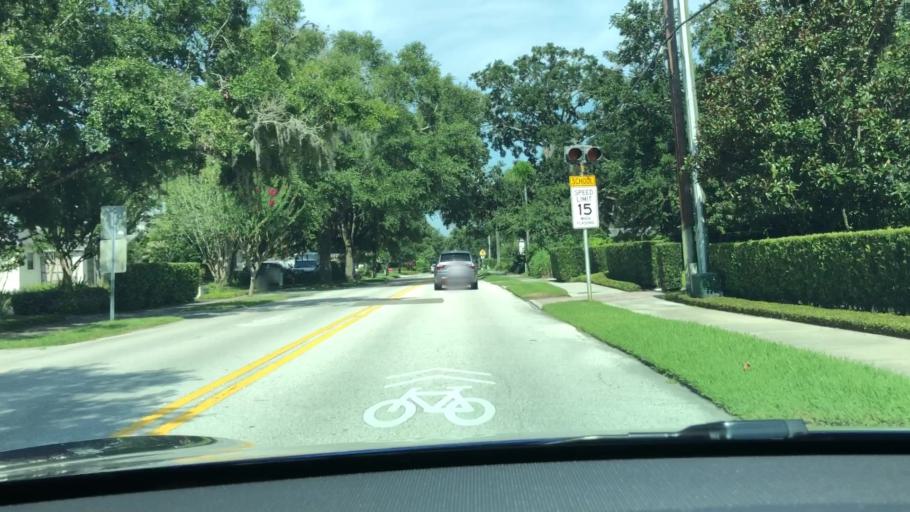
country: US
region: Florida
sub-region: Orange County
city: Winter Park
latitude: 28.6089
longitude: -81.3302
